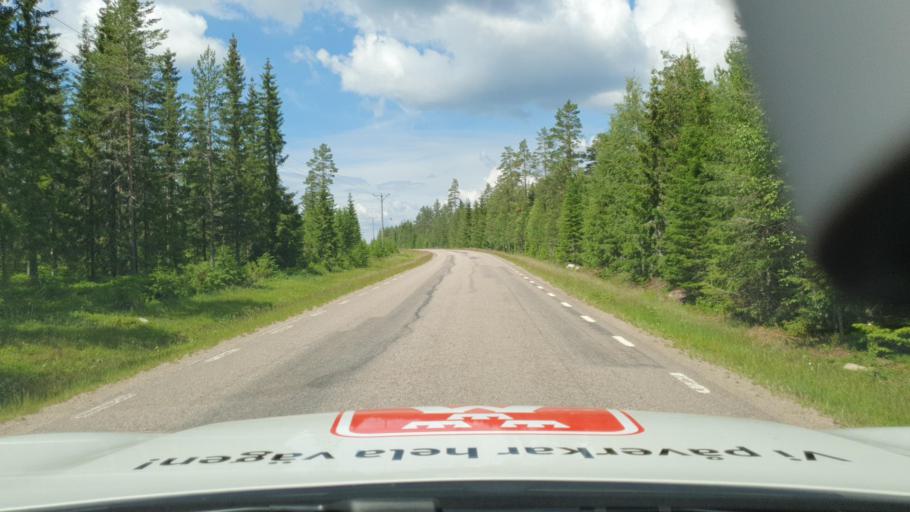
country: SE
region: Vaermland
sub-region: Torsby Kommun
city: Torsby
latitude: 60.4943
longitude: 12.8671
